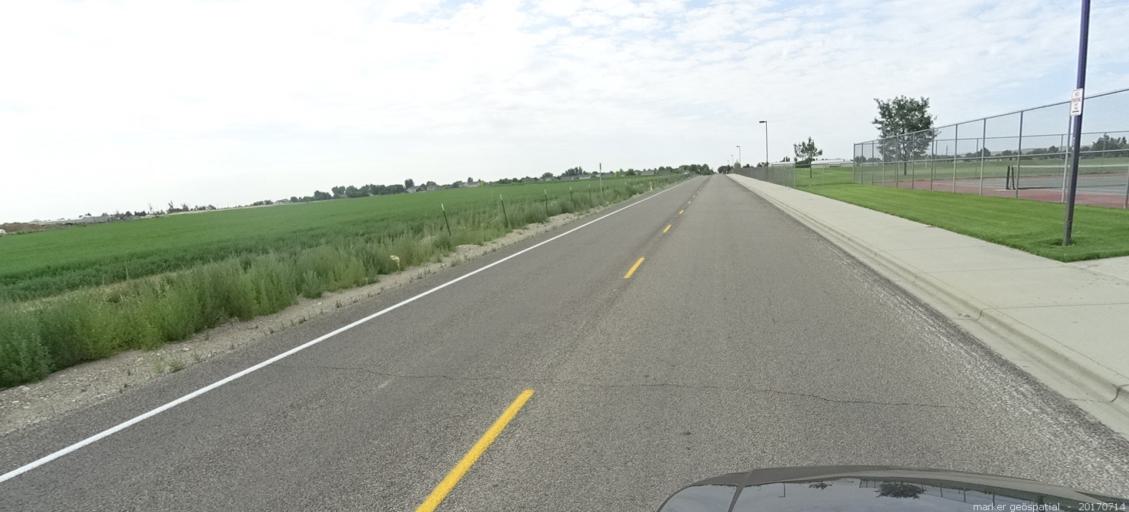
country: US
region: Idaho
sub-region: Ada County
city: Kuna
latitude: 43.5008
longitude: -116.4039
